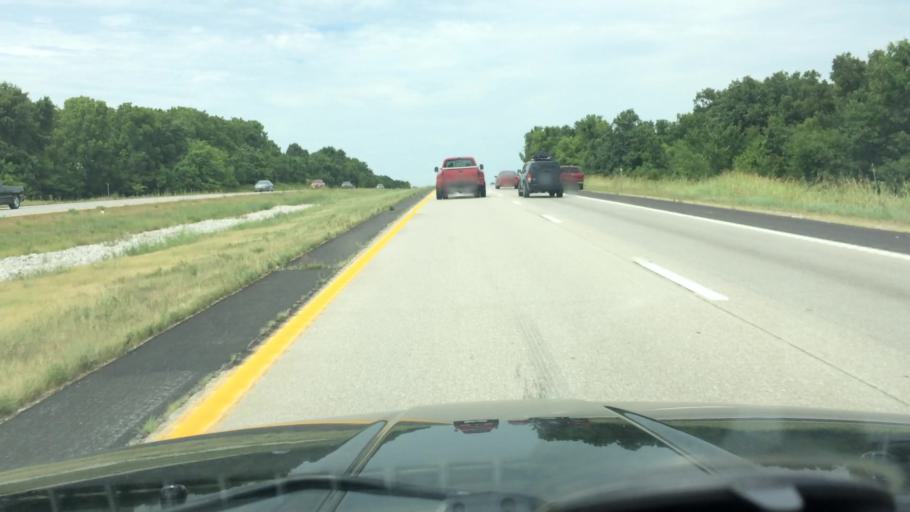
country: US
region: Missouri
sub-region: Greene County
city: Willard
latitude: 37.4423
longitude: -93.3553
